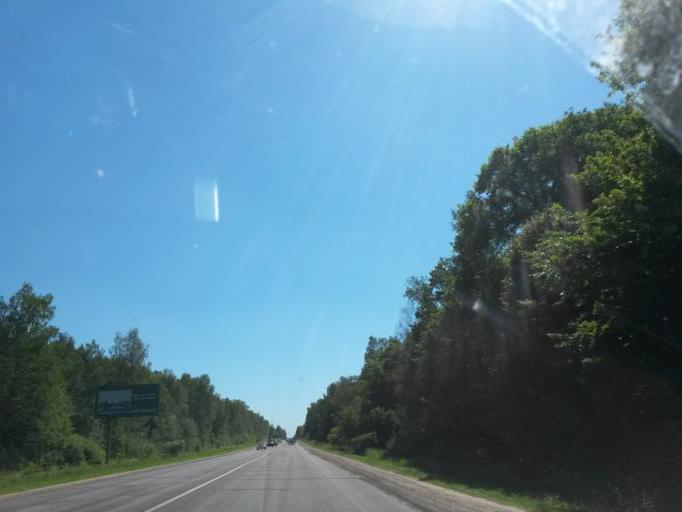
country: RU
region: Moskovskaya
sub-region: Chekhovskiy Rayon
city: Chekhov
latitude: 55.0873
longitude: 37.4415
